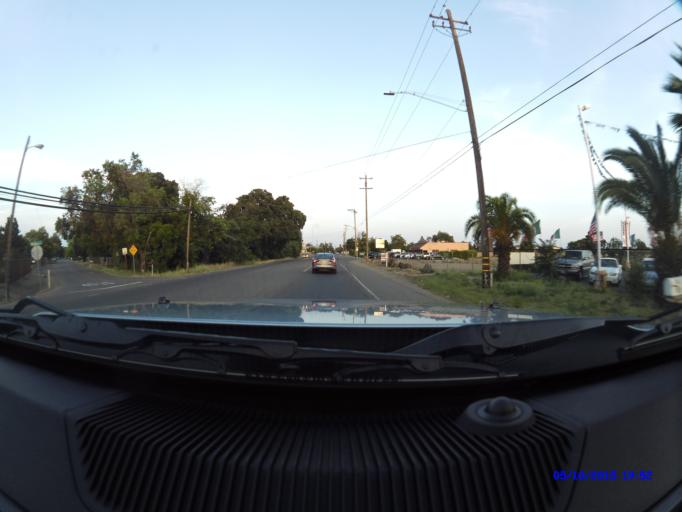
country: US
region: California
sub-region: San Joaquin County
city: Kennedy
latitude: 37.9435
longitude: -121.2534
